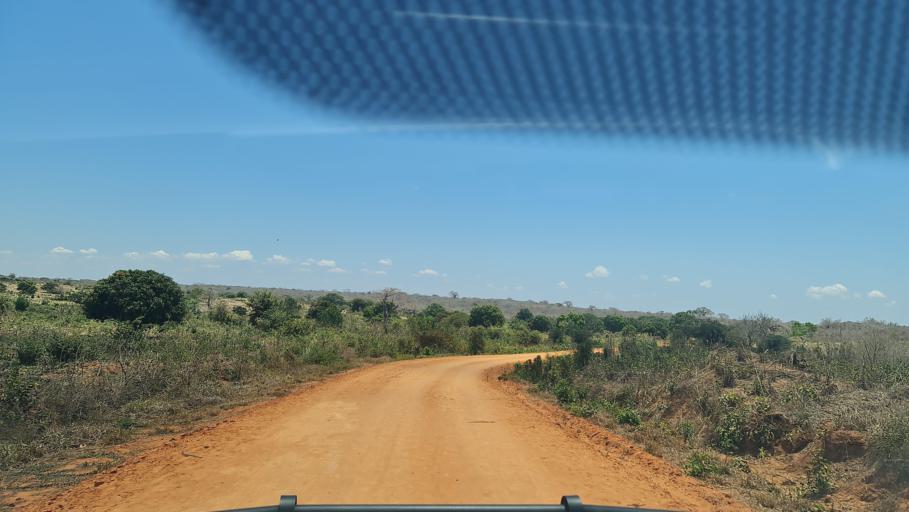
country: MZ
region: Nampula
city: Nacala
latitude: -14.2135
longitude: 40.6793
